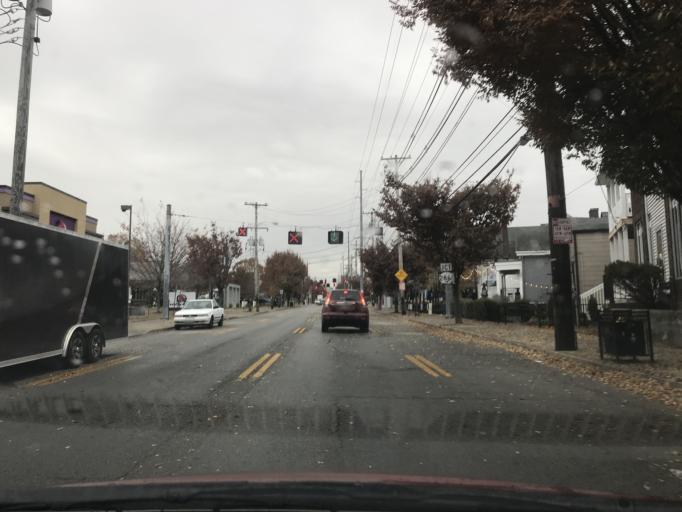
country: US
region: Kentucky
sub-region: Jefferson County
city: Audubon Park
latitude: 38.2392
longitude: -85.7223
